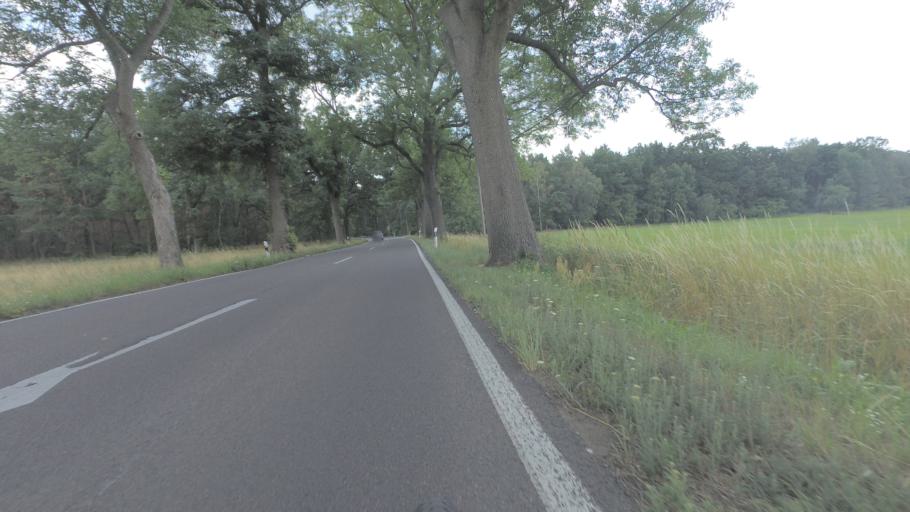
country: DE
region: Brandenburg
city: Sperenberg
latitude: 52.1776
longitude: 13.3191
